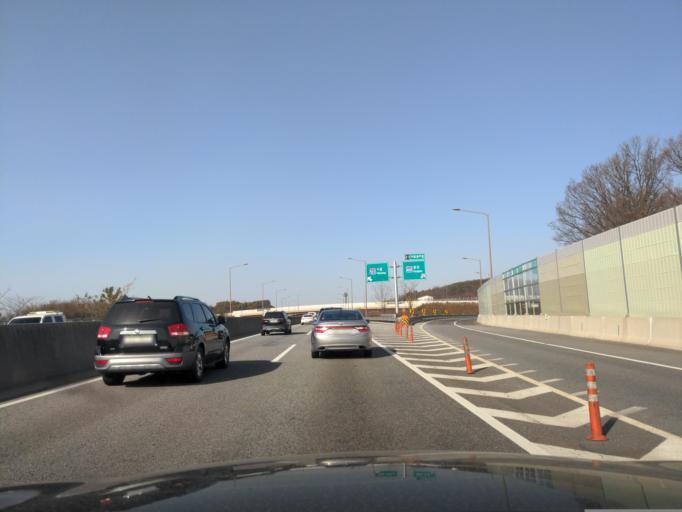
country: KR
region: Gyeonggi-do
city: Hwaseong-si
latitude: 37.1844
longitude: 126.7780
